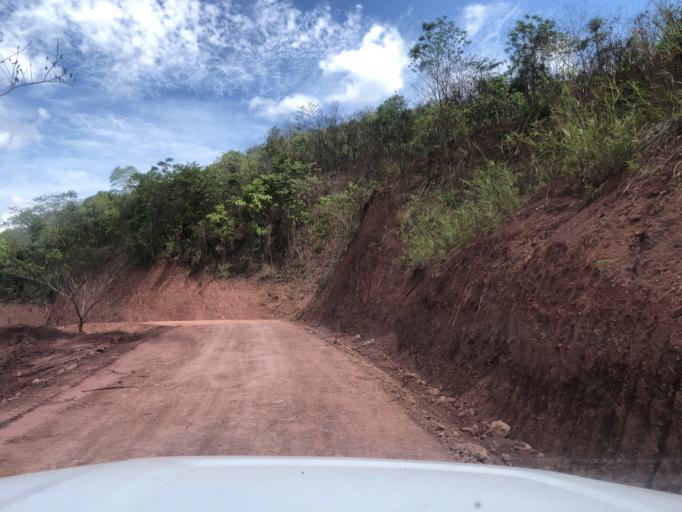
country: CN
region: Yunnan
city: Menglie
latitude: 22.2264
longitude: 101.6280
